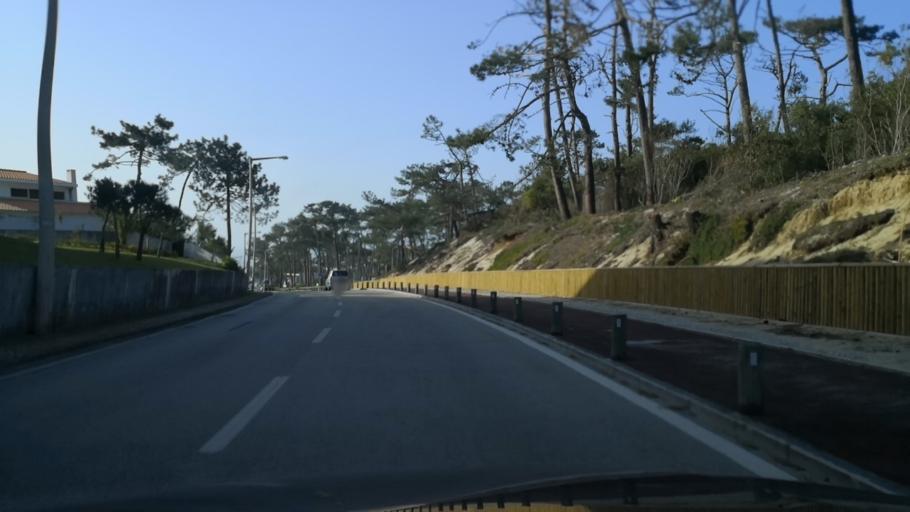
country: PT
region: Leiria
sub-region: Alcobaca
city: Pataias
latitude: 39.7562
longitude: -9.0262
